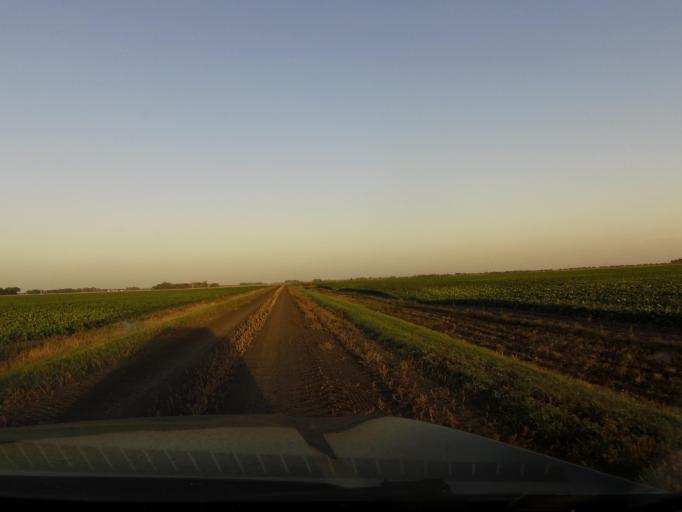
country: US
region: North Dakota
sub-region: Walsh County
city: Grafton
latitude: 48.3831
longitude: -97.2427
